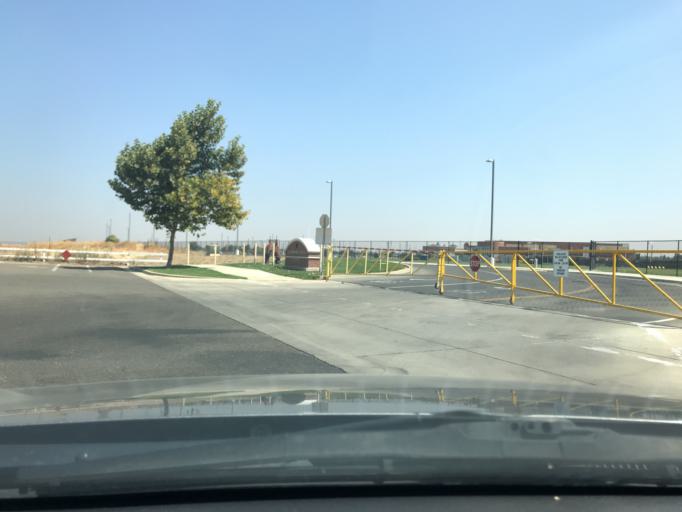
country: US
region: California
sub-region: Merced County
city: Merced
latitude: 37.3639
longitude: -120.4732
